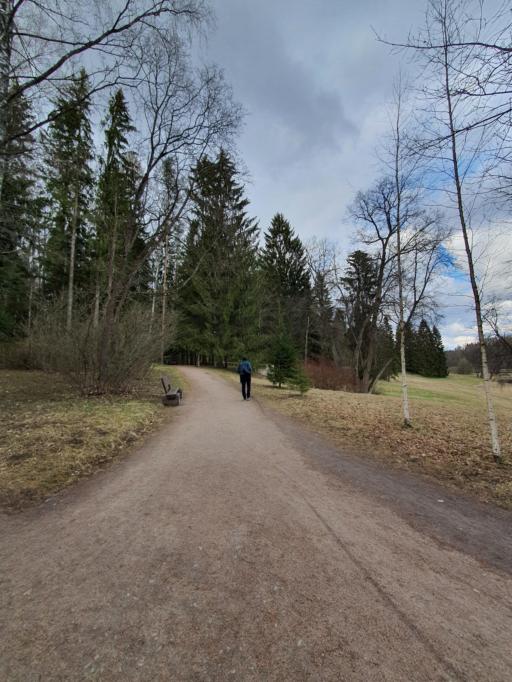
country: RU
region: St.-Petersburg
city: Tyarlevo
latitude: 59.6889
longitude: 30.4546
